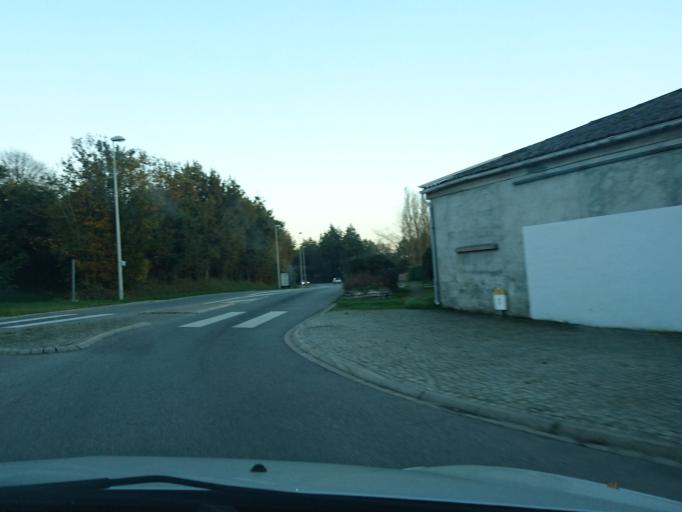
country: FR
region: Brittany
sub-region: Departement du Finistere
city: Saint-Renan
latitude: 48.4353
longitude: -4.6187
